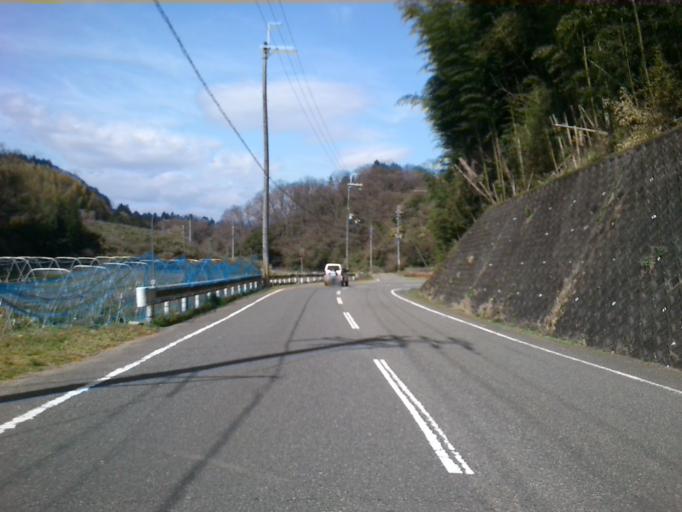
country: JP
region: Nara
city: Nara-shi
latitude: 34.7209
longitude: 135.8782
